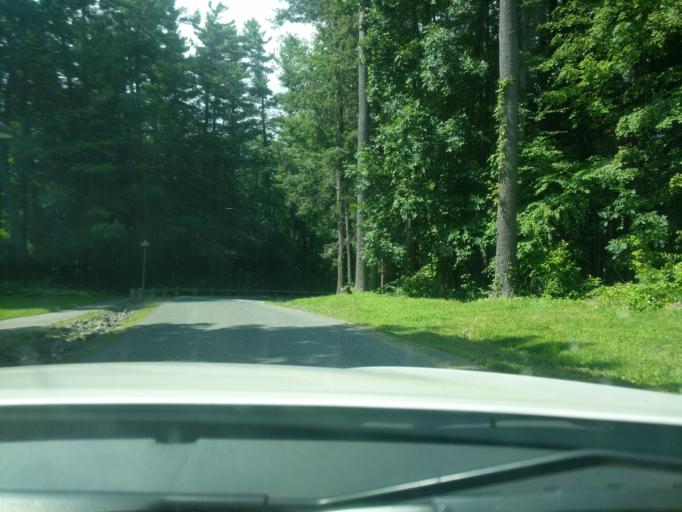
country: US
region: Massachusetts
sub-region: Berkshire County
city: Great Barrington
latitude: 42.2083
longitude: -73.3720
